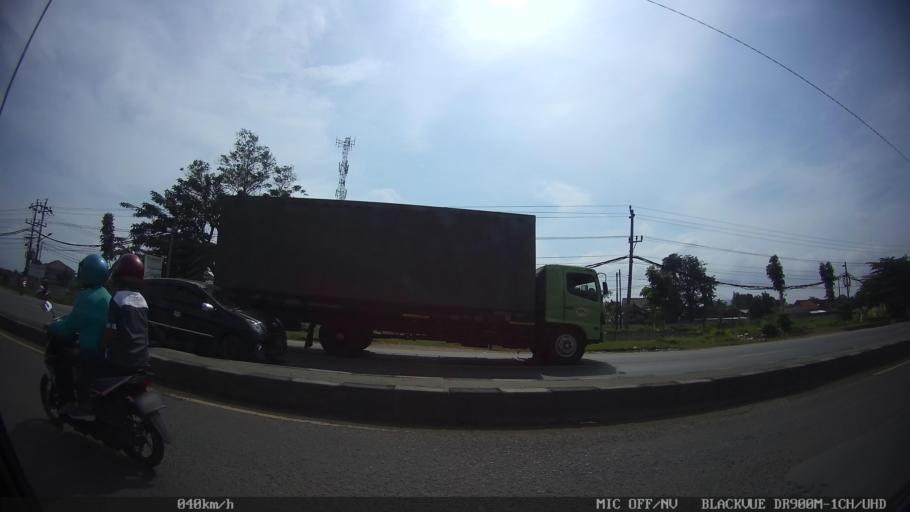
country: ID
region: Lampung
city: Kedaton
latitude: -5.3844
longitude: 105.2866
